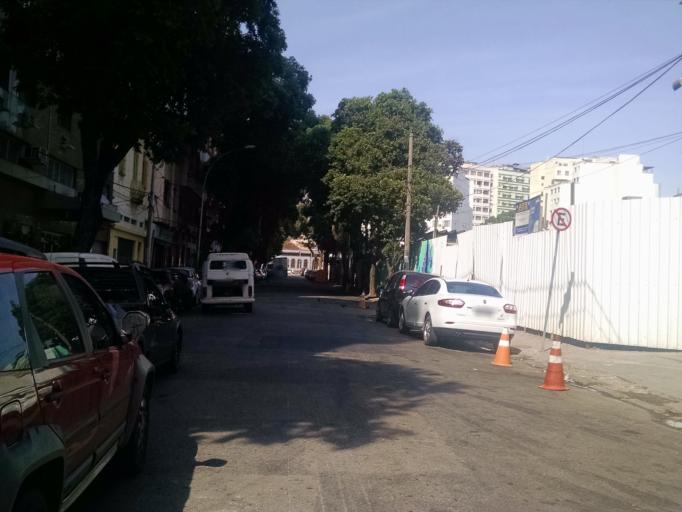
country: BR
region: Rio de Janeiro
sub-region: Rio De Janeiro
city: Rio de Janeiro
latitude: -22.9131
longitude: -43.1884
